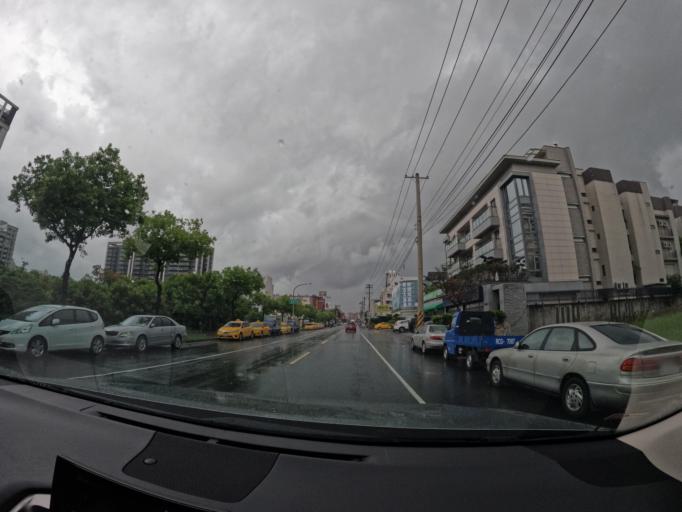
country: TW
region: Taiwan
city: Fengshan
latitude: 22.6514
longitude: 120.3415
